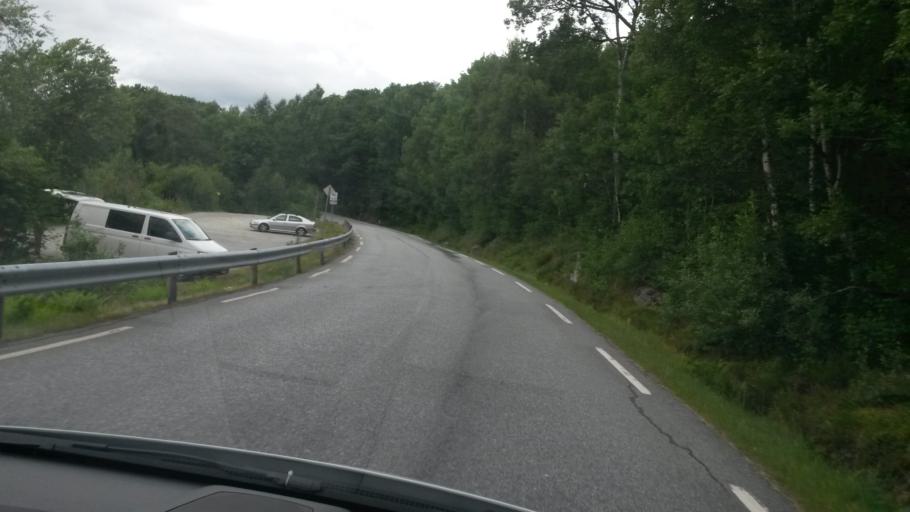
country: NO
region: Rogaland
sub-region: Sandnes
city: Sandnes
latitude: 58.8863
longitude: 5.7770
